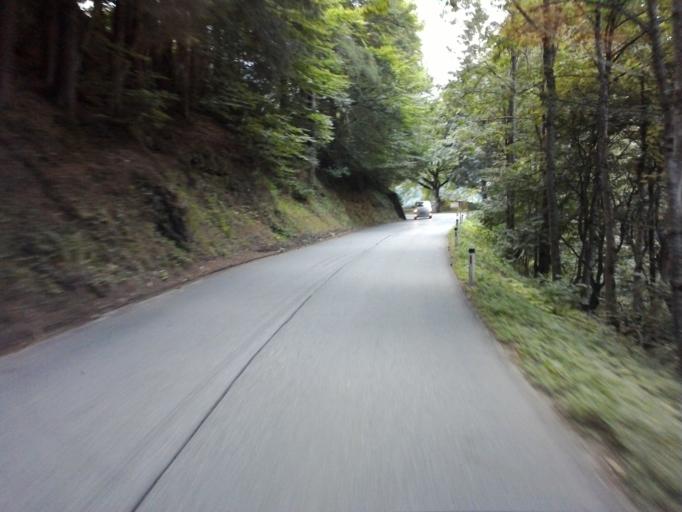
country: AT
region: Carinthia
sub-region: Politischer Bezirk Spittal an der Drau
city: Oberdrauburg
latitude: 46.6781
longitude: 12.9630
